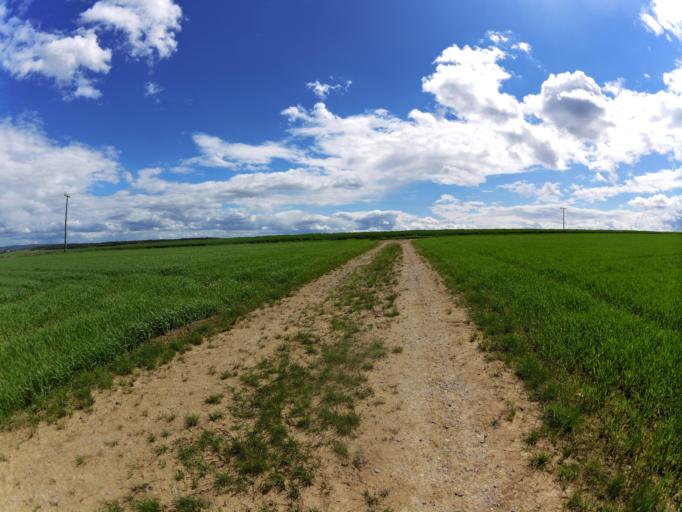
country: DE
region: Bavaria
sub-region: Regierungsbezirk Unterfranken
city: Volkach
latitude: 49.8779
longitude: 10.2401
